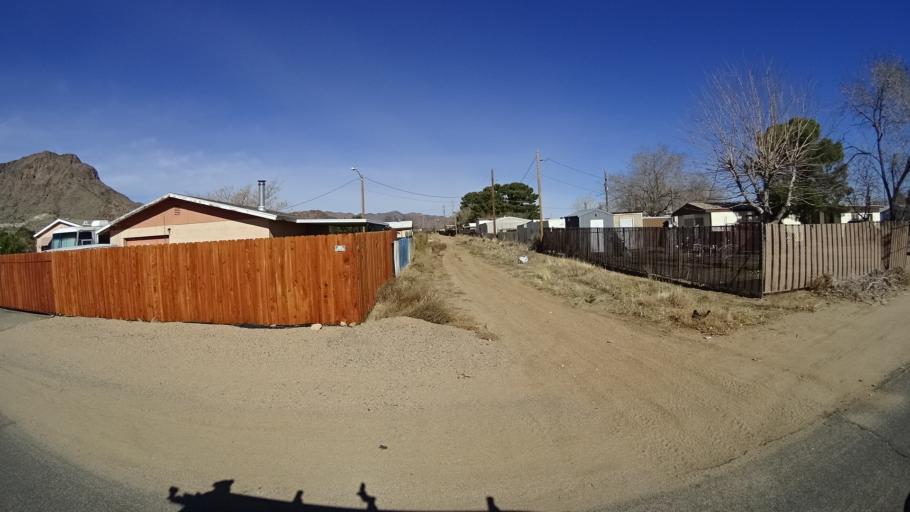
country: US
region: Arizona
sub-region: Mohave County
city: New Kingman-Butler
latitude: 35.2706
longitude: -114.0437
